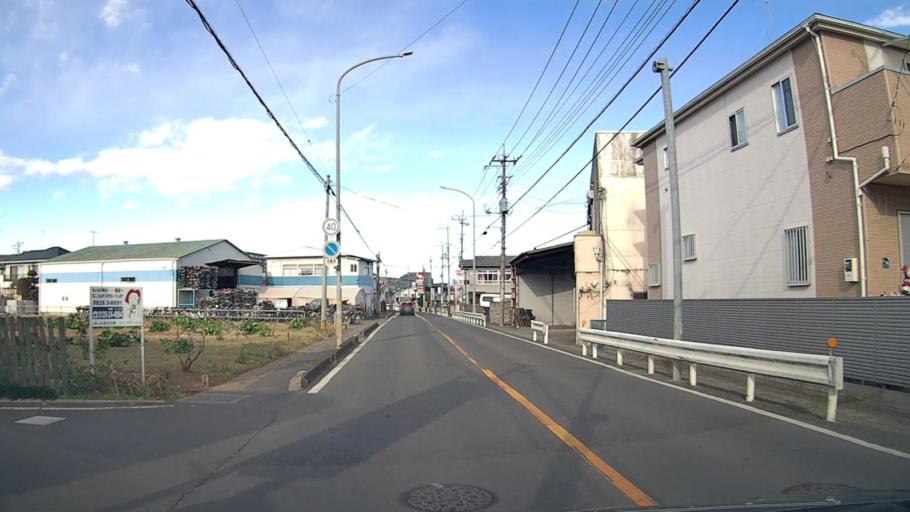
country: JP
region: Saitama
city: Asaka
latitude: 35.7890
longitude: 139.5756
